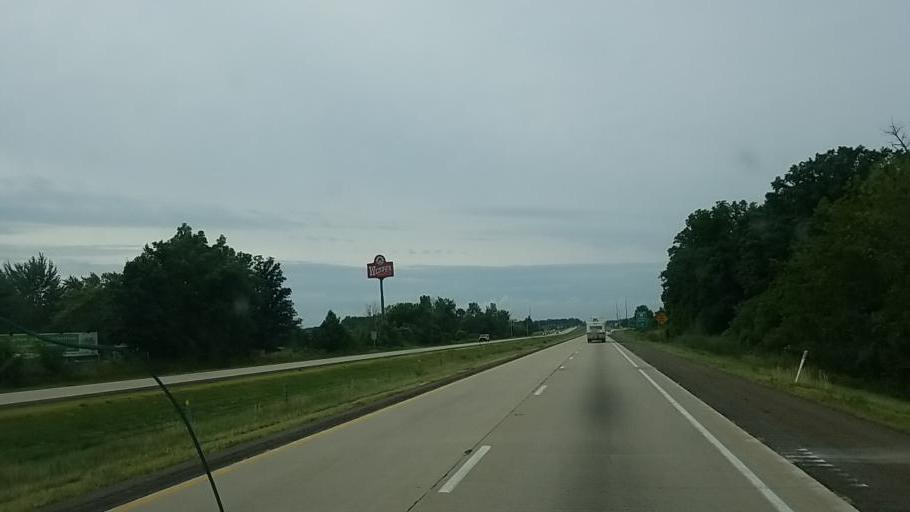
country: US
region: Indiana
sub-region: DeKalb County
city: Auburn
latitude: 41.3745
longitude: -85.0778
